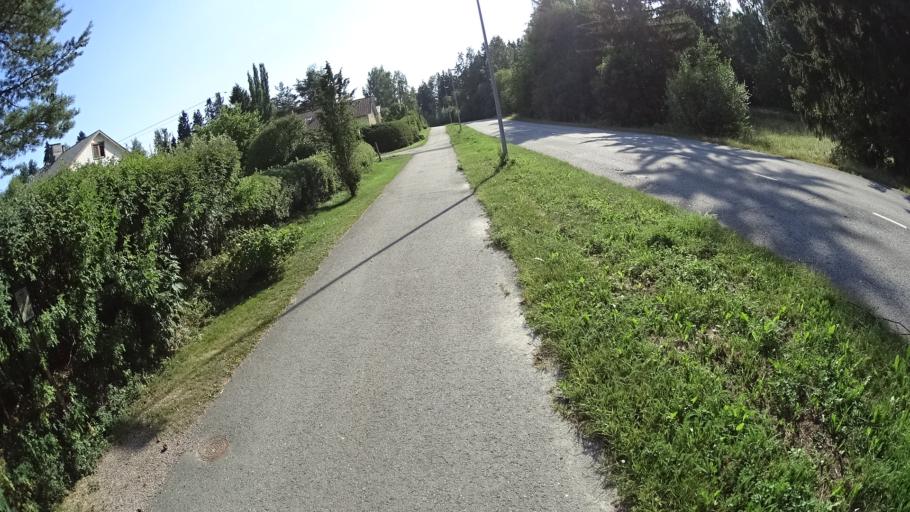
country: FI
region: Uusimaa
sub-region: Porvoo
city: Porvoo
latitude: 60.4124
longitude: 25.6517
